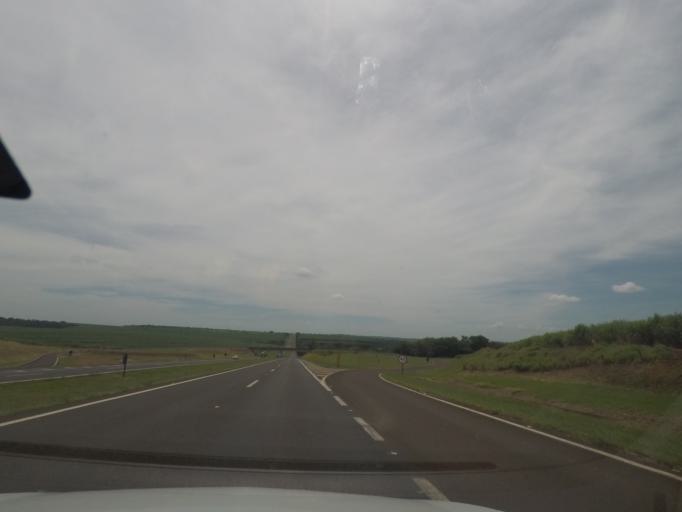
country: BR
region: Sao Paulo
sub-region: Bebedouro
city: Bebedouro
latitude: -21.0413
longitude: -48.4172
